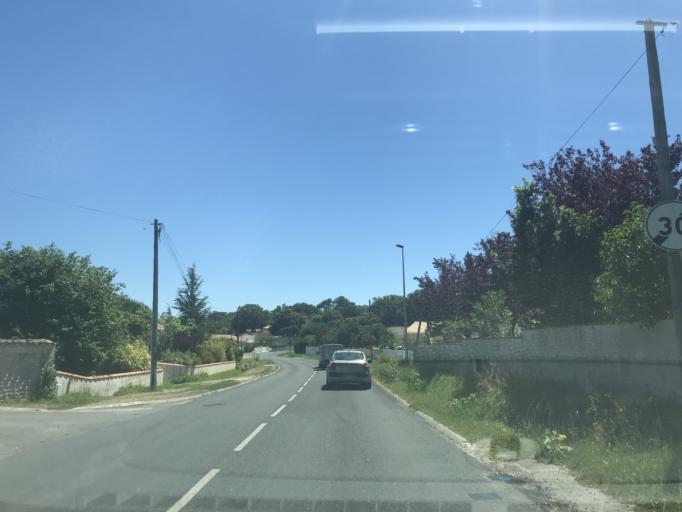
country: FR
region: Poitou-Charentes
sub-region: Departement de la Charente-Maritime
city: Meschers-sur-Gironde
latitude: 45.5713
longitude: -0.9608
